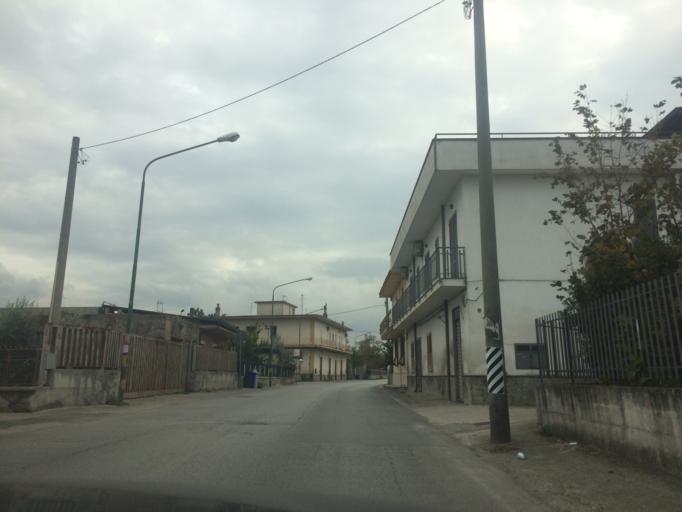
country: IT
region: Campania
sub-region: Provincia di Napoli
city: Piazzolla
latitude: 40.8999
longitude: 14.5304
